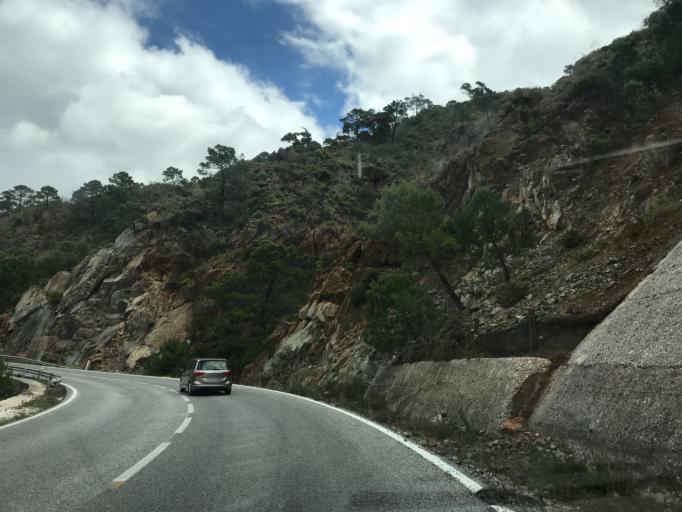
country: ES
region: Andalusia
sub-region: Provincia de Malaga
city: Benahavis
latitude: 36.5637
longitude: -5.0590
